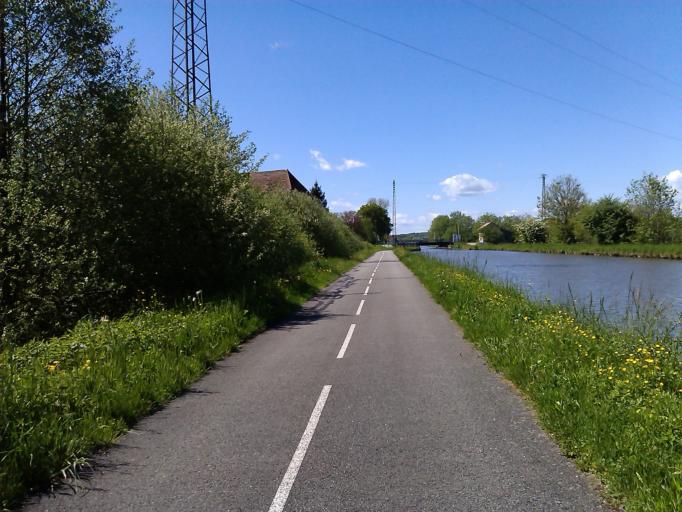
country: FR
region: Franche-Comte
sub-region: Territoire de Belfort
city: Morvillars
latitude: 47.5674
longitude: 6.9462
